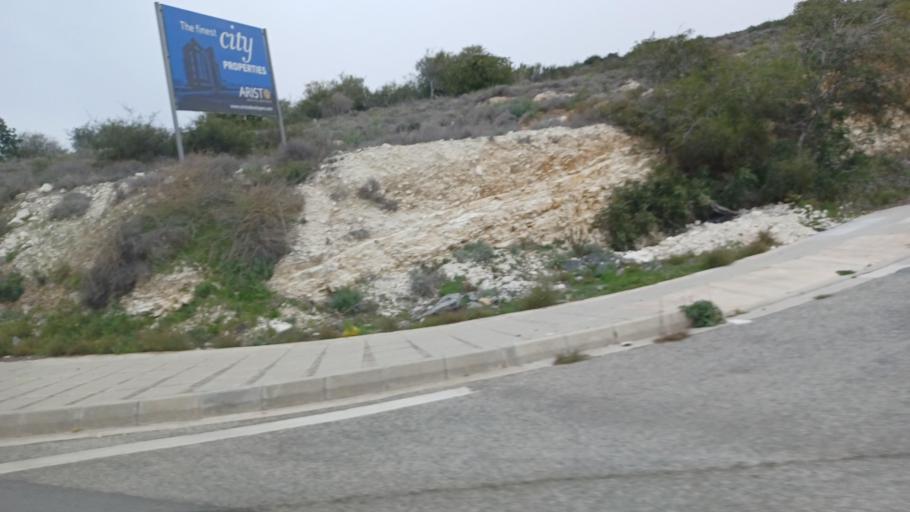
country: CY
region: Pafos
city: Paphos
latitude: 34.7699
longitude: 32.4588
